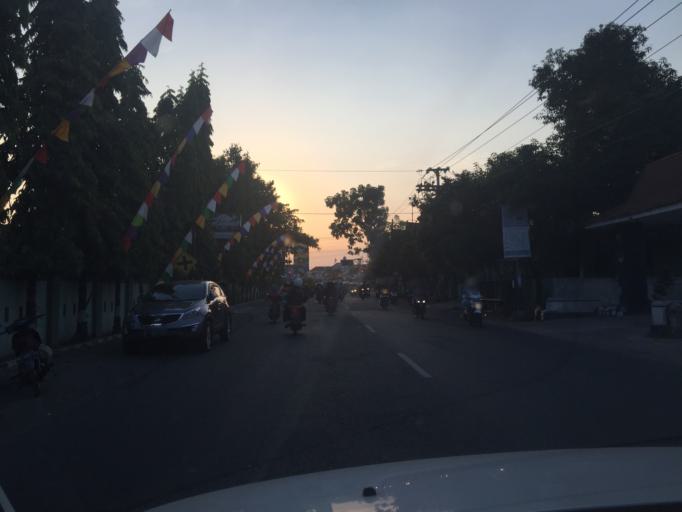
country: ID
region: Daerah Istimewa Yogyakarta
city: Gamping Lor
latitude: -7.7774
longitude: 110.3329
